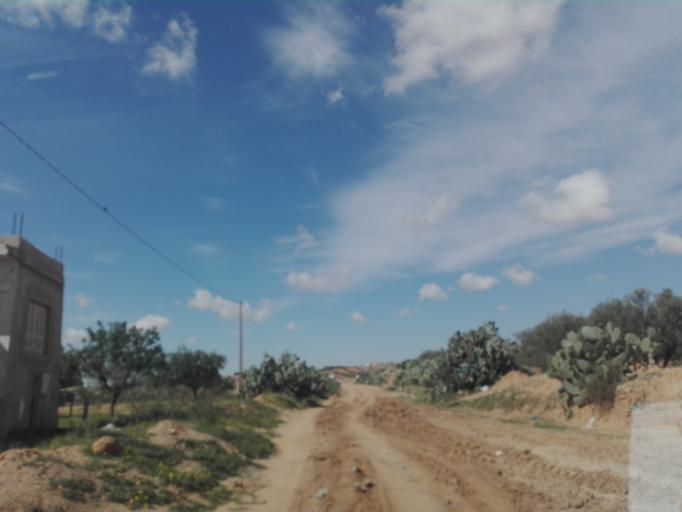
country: TN
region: Safaqis
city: Sfax
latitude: 34.7327
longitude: 10.5105
